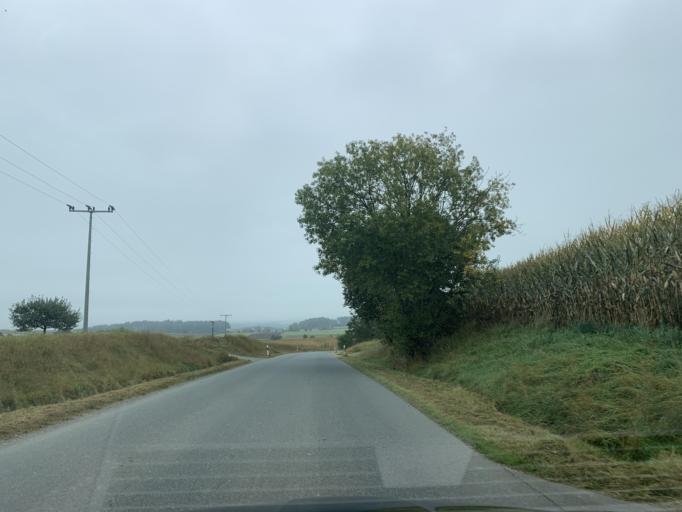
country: DE
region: Bavaria
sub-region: Upper Palatinate
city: Winklarn
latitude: 49.4075
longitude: 12.4692
